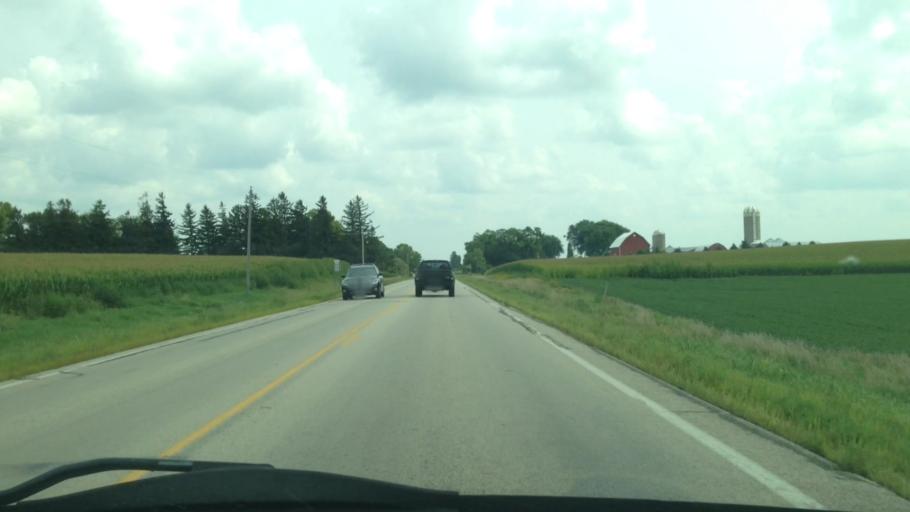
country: US
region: Minnesota
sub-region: Wabasha County
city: Elgin
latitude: 44.1368
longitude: -92.3581
